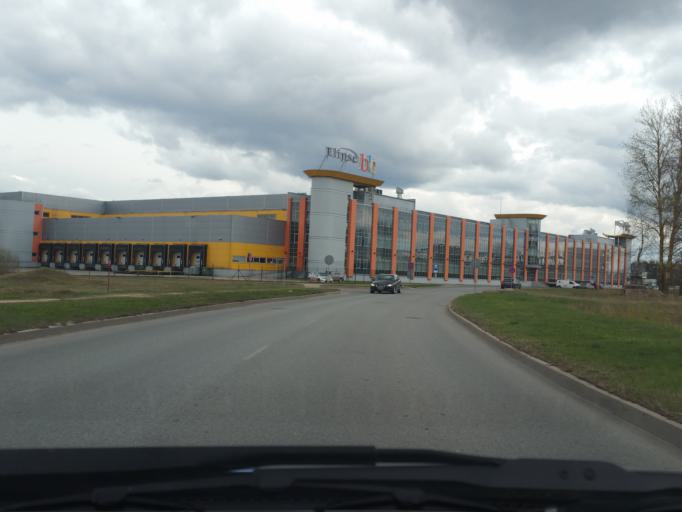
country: LV
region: Marupe
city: Marupe
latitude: 56.9270
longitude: 23.9914
